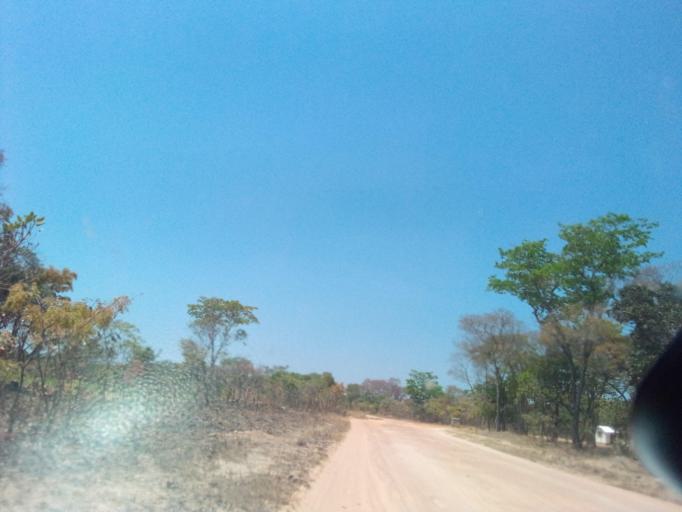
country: ZM
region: Northern
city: Mpika
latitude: -12.2442
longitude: 30.6642
